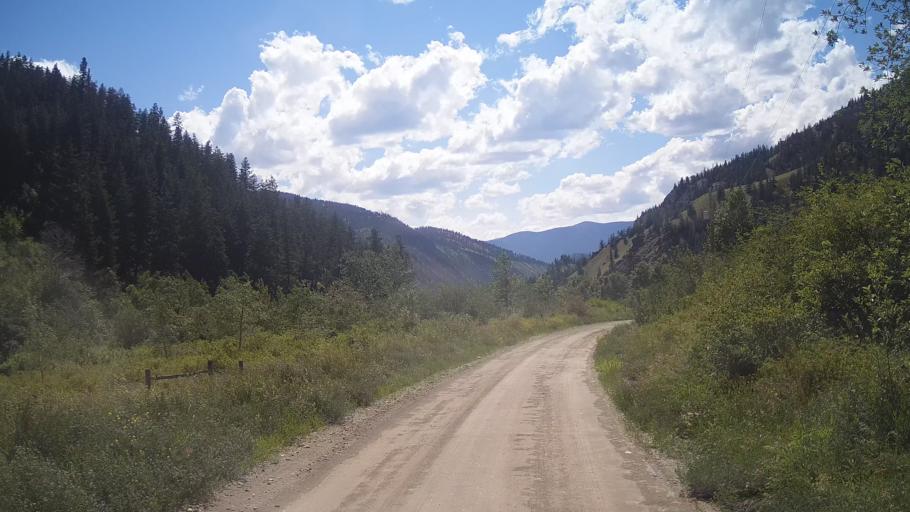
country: CA
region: British Columbia
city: Lillooet
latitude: 51.2394
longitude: -122.0439
